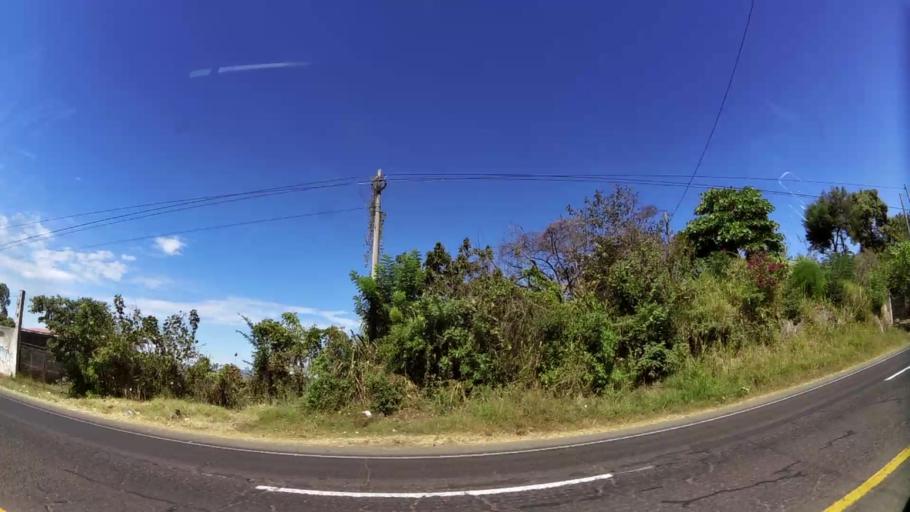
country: SV
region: Ahuachapan
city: Atiquizaya
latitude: 13.9721
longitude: -89.7263
